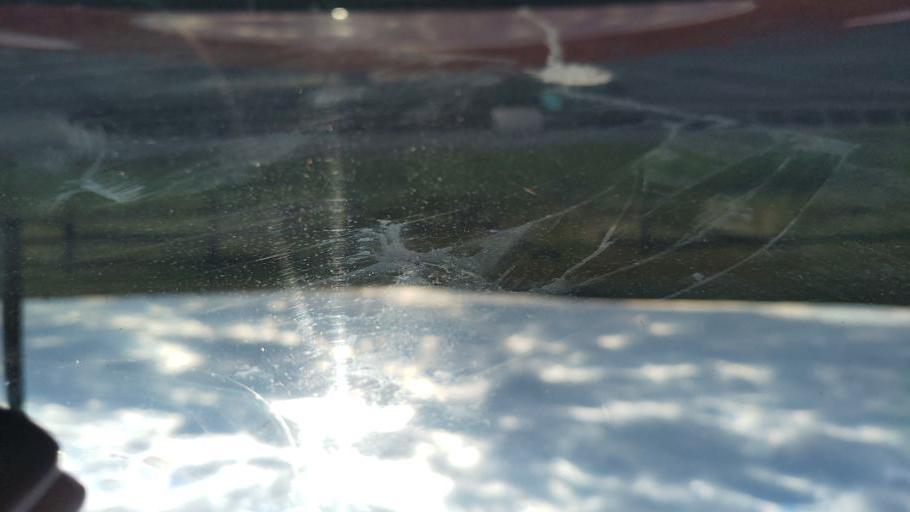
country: GB
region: England
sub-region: Blackburn with Darwen
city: Darwen
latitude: 53.6664
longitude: -2.5096
